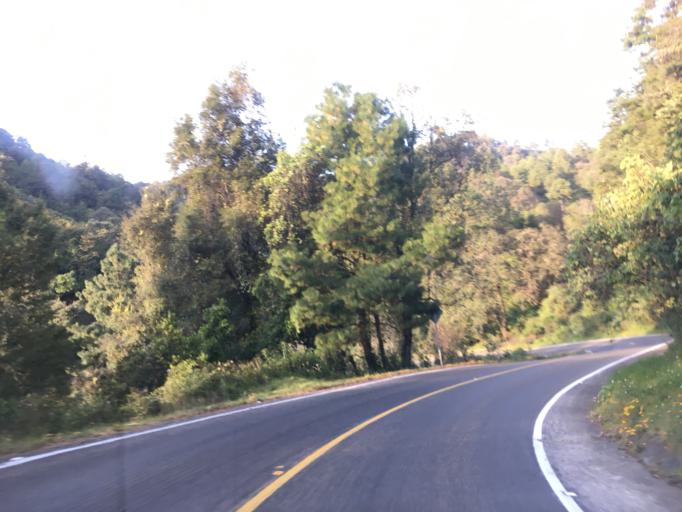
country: MX
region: Michoacan
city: Tzitzio
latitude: 19.6713
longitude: -100.9170
